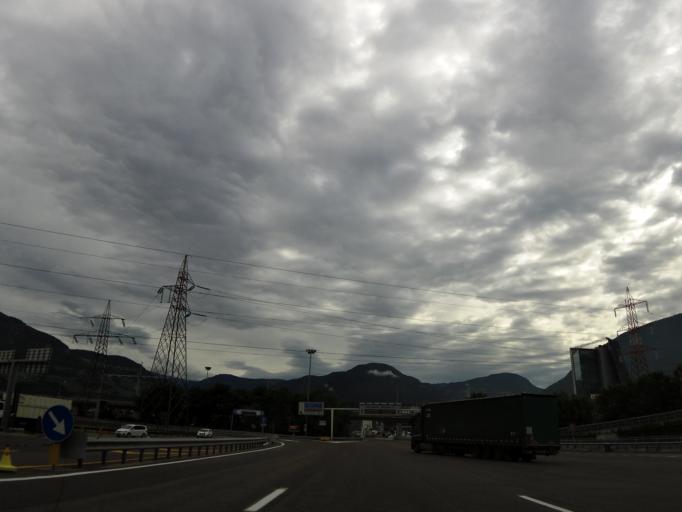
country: IT
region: Trentino-Alto Adige
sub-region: Bolzano
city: San Giacomo
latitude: 46.4753
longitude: 11.3203
